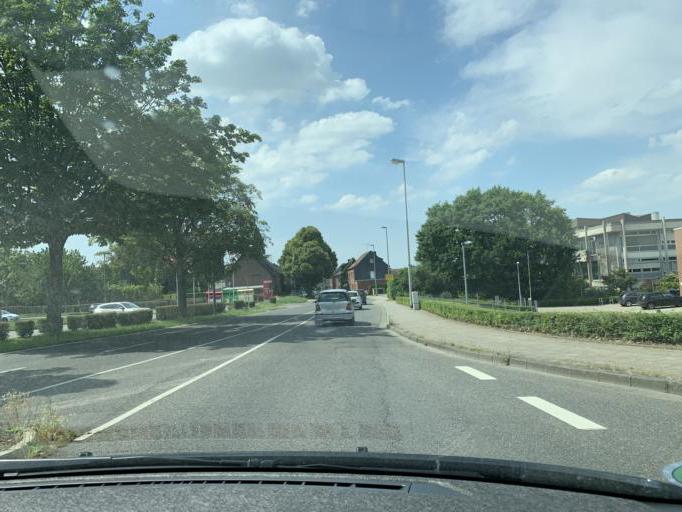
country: DE
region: North Rhine-Westphalia
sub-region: Regierungsbezirk Dusseldorf
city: Grevenbroich
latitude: 51.0417
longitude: 6.5850
